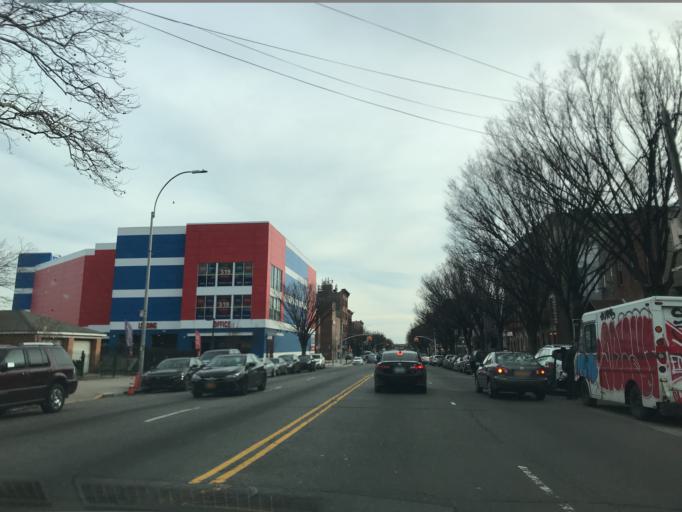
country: US
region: New York
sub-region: Kings County
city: East New York
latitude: 40.6732
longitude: -73.8962
